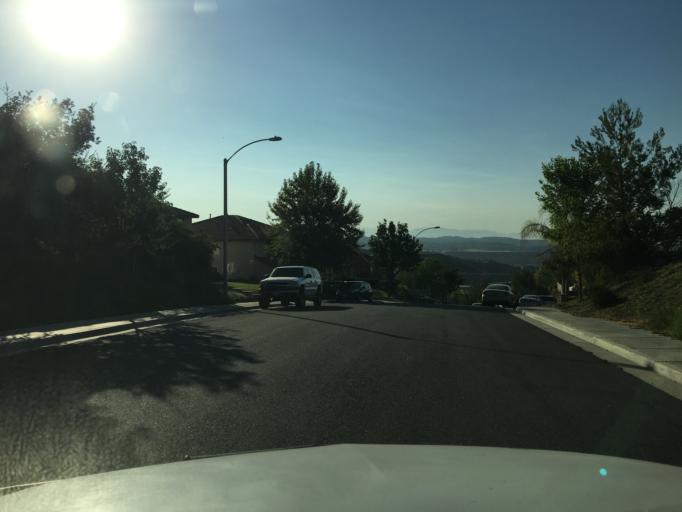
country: US
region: California
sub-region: Los Angeles County
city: Castaic
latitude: 34.5105
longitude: -118.6392
